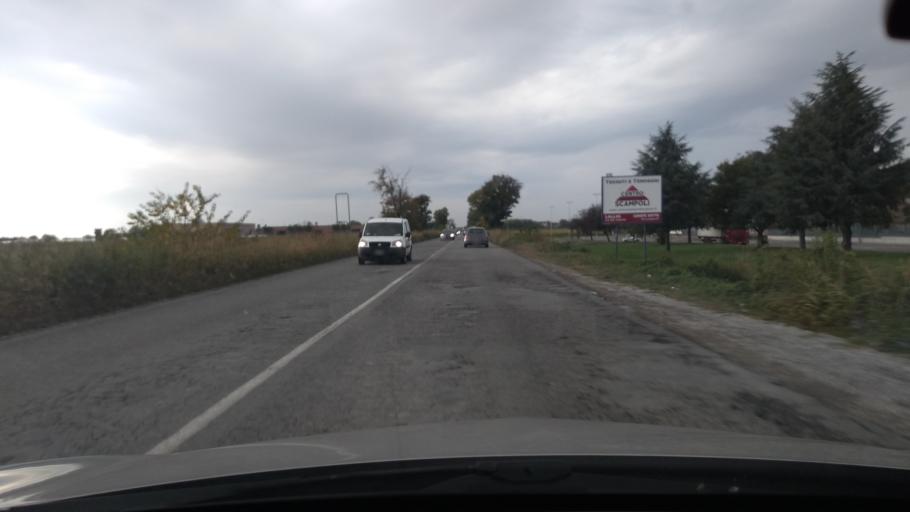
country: IT
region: Lombardy
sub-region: Provincia di Bergamo
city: Spirano
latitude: 45.5934
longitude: 9.6637
